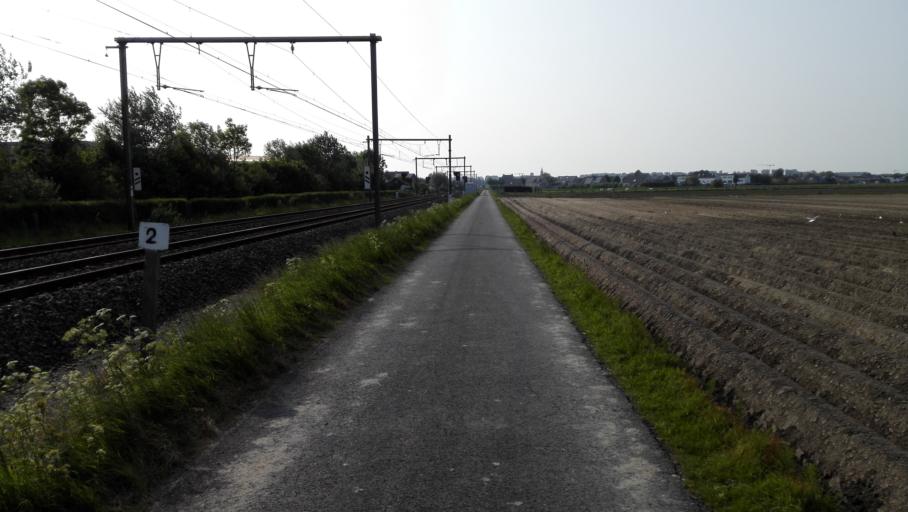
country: BE
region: Flanders
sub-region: Provincie West-Vlaanderen
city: Blankenberge
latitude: 51.2994
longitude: 3.1545
